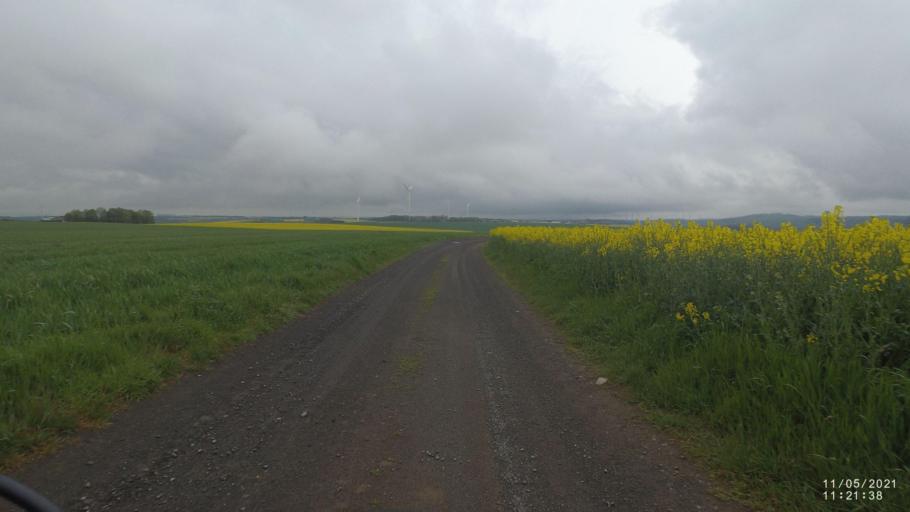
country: DE
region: Rheinland-Pfalz
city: Monreal
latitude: 50.3094
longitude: 7.1894
